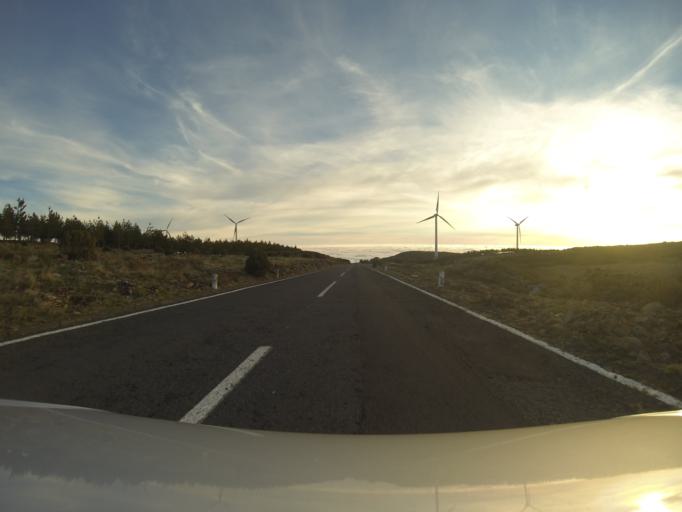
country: PT
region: Madeira
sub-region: Sao Vicente
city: Sao Vicente
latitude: 32.7403
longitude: -17.0589
